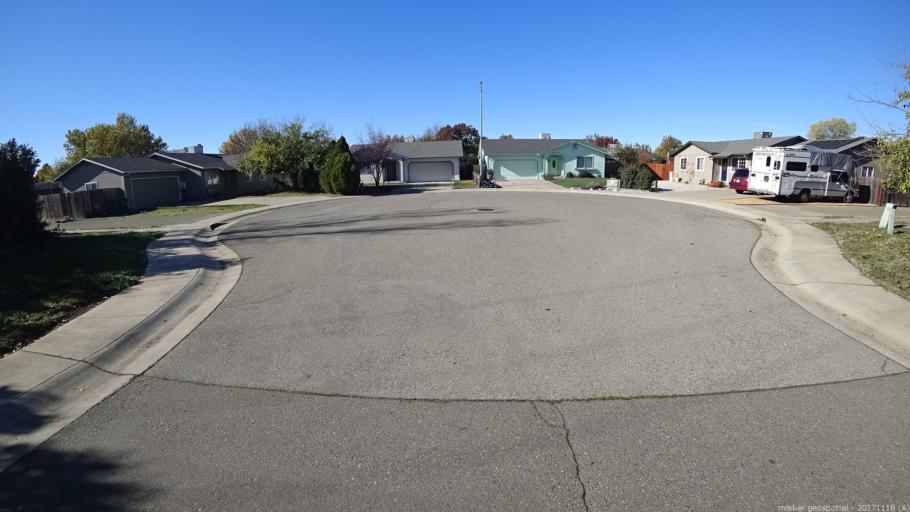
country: US
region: California
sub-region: Shasta County
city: Cottonwood
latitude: 40.3937
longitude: -122.2772
